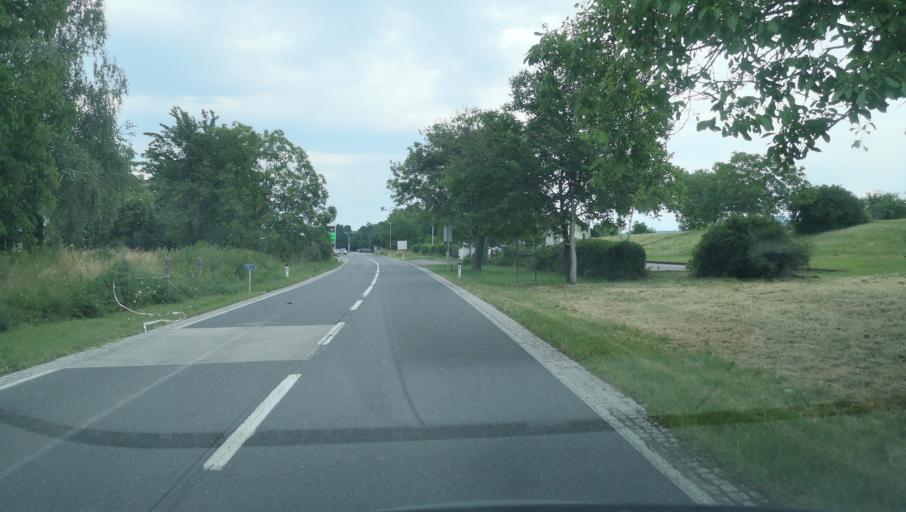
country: AT
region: Lower Austria
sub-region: Politischer Bezirk Melk
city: Klein-Poechlarn
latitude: 48.2171
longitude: 15.2193
